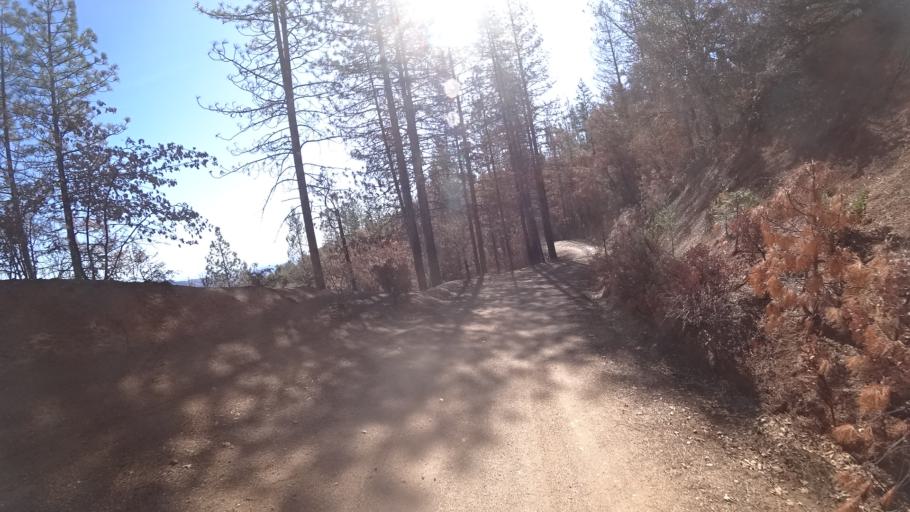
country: US
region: California
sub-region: Tehama County
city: Rancho Tehama Reserve
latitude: 39.6758
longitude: -122.7023
